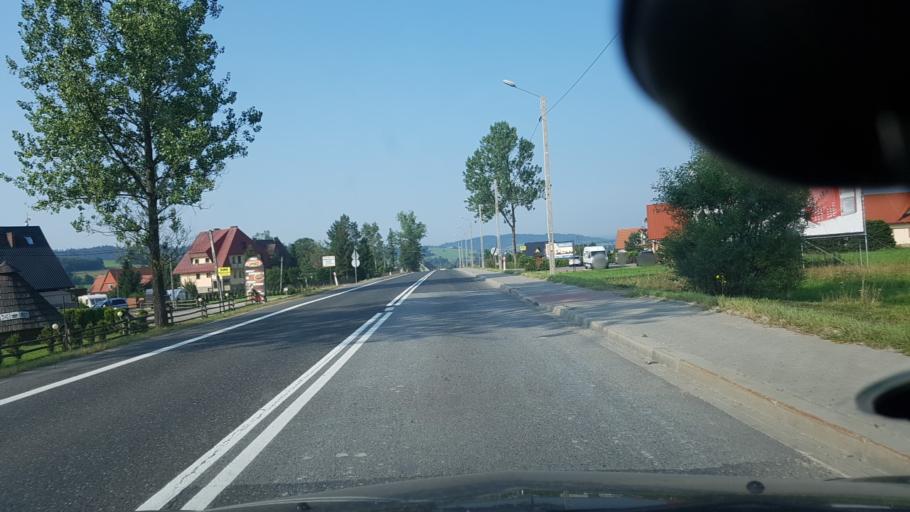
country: PL
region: Lesser Poland Voivodeship
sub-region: Powiat nowotarski
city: Podwilk
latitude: 49.5566
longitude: 19.7588
